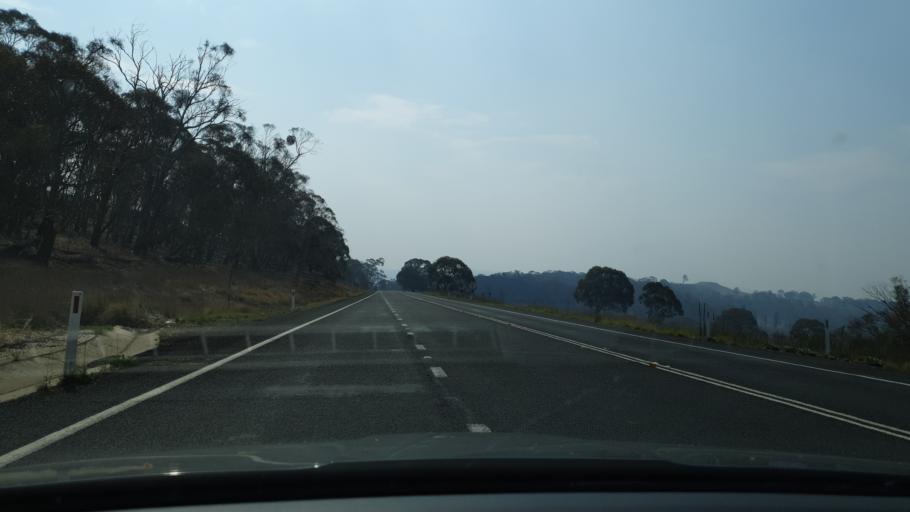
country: AU
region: New South Wales
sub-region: Guyra
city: Guyra
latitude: -29.9934
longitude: 151.7220
